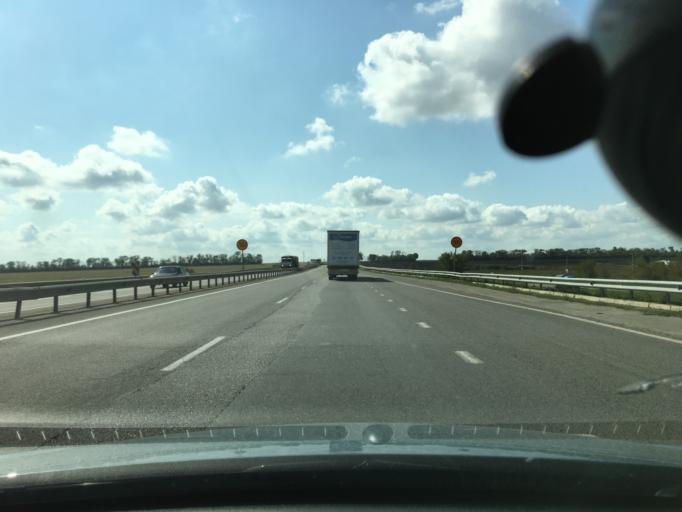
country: RU
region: Krasnodarskiy
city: Krasnoye
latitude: 46.7326
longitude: 39.6563
